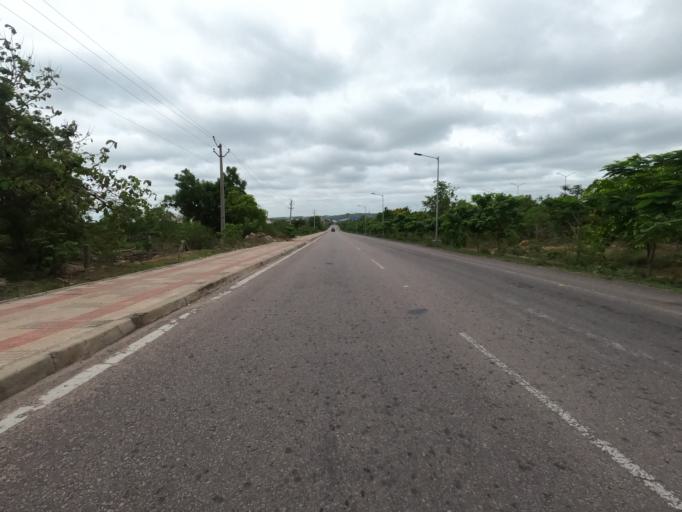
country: IN
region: Telangana
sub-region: Hyderabad
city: Hyderabad
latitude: 17.3457
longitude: 78.3629
